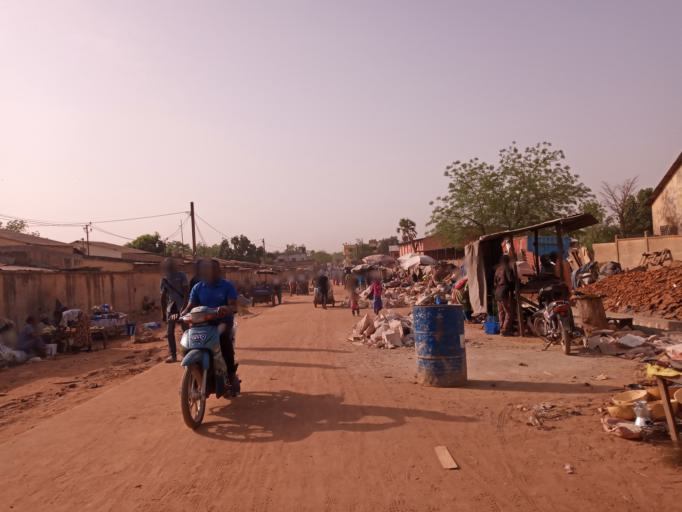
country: ML
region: Bamako
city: Bamako
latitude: 12.6577
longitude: -7.9898
